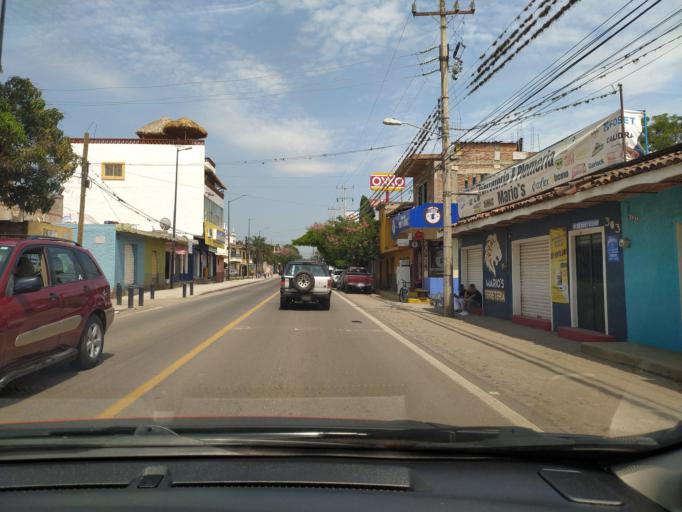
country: MX
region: Jalisco
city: San Juan Cosala
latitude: 20.2891
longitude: -103.3475
